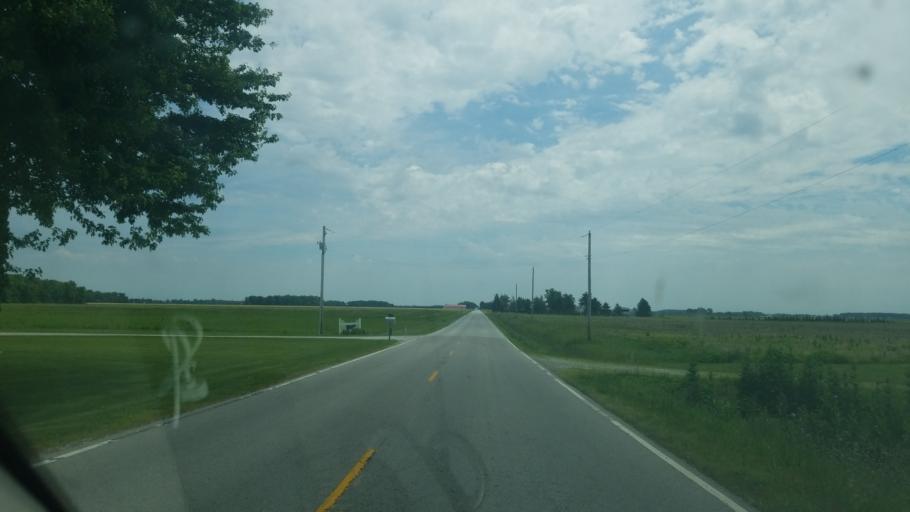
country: US
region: Ohio
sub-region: Wood County
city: Bowling Green
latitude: 41.2967
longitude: -83.6260
